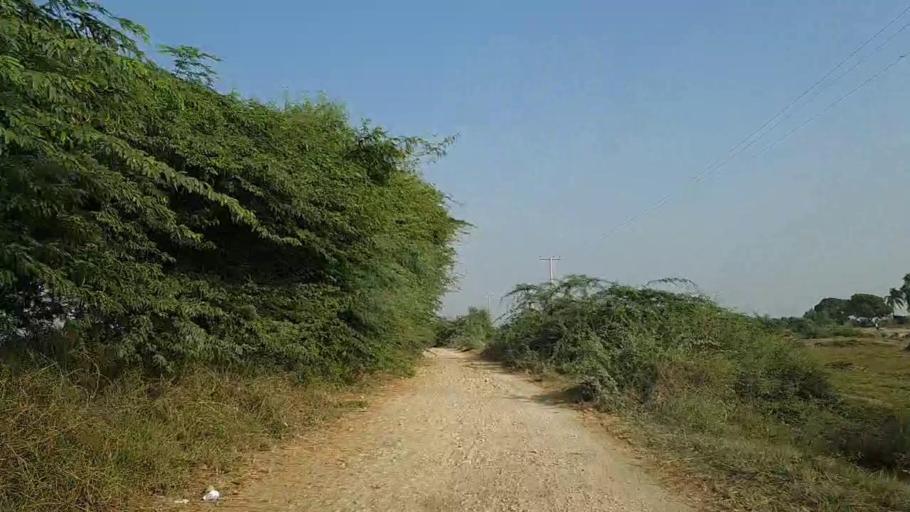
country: PK
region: Sindh
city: Mirpur Sakro
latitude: 24.6161
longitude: 67.7365
